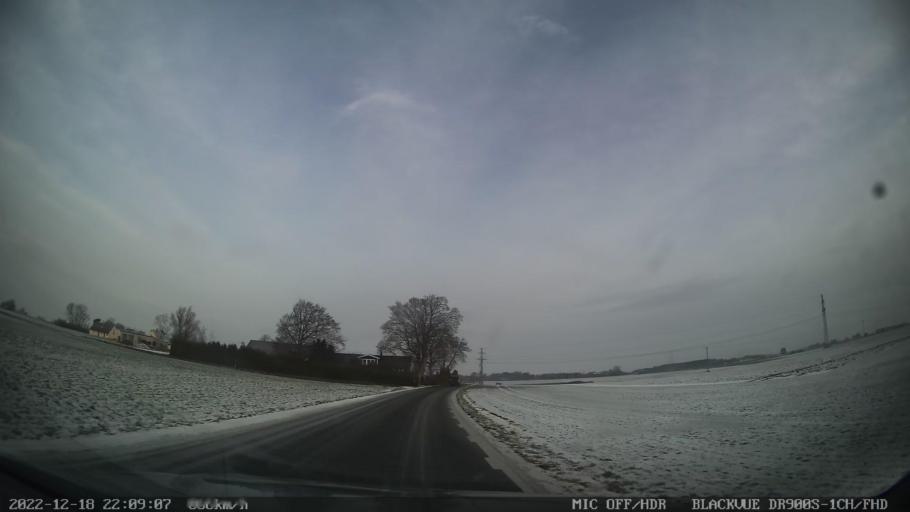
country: SE
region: Skane
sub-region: Tomelilla Kommun
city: Tomelilla
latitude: 55.5306
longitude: 14.0419
